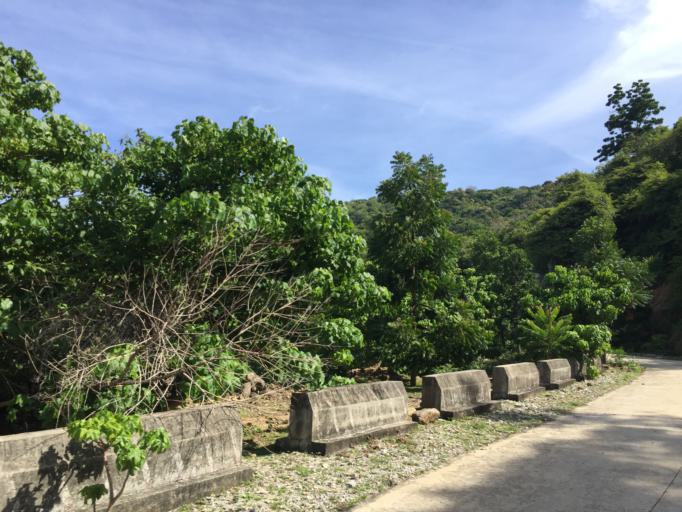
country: VN
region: Quang Nam
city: Hoi An
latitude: 15.9310
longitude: 108.5314
